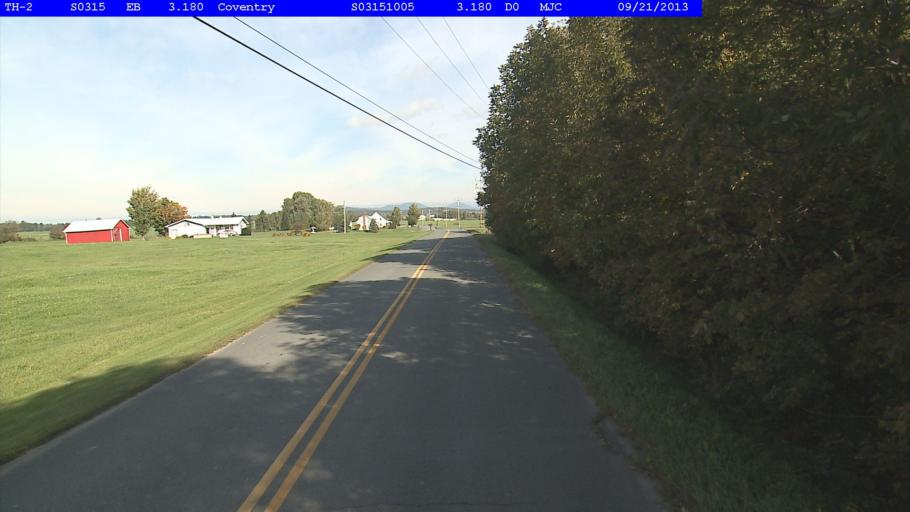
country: US
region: Vermont
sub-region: Orleans County
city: Newport
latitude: 44.8818
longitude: -72.2181
